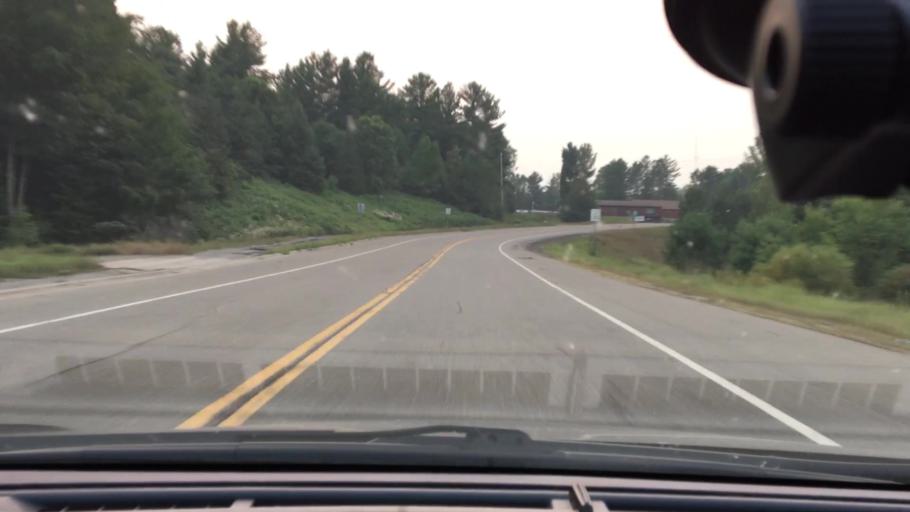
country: US
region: Minnesota
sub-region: Crow Wing County
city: Cross Lake
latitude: 46.8196
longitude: -93.9459
